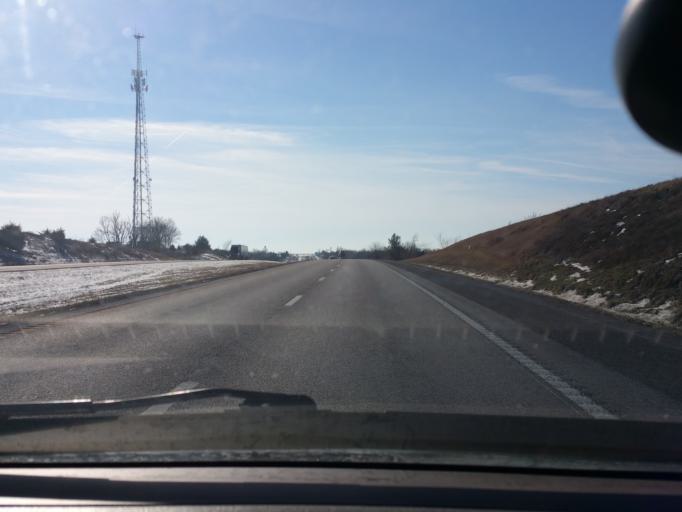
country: US
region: Missouri
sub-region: Clinton County
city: Cameron
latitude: 39.8717
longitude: -94.1688
